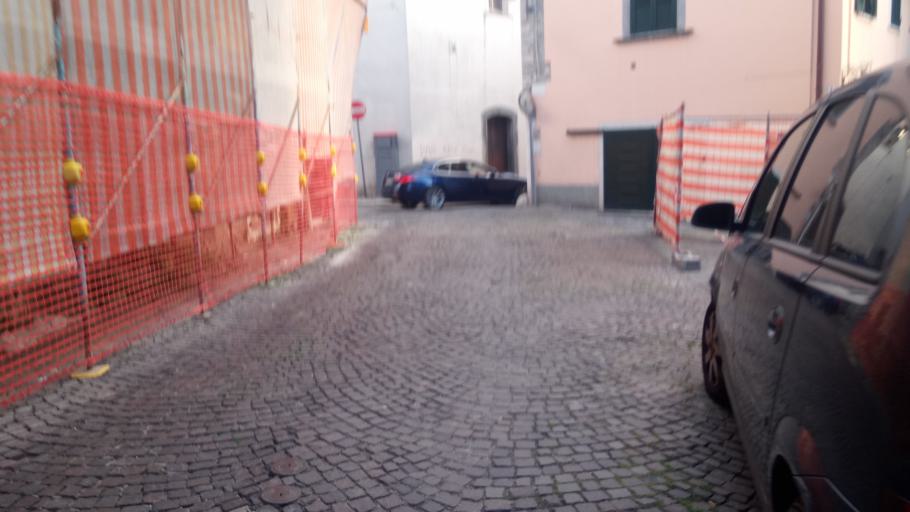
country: IT
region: Basilicate
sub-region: Provincia di Potenza
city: Melfi
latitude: 40.9975
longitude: 15.6584
